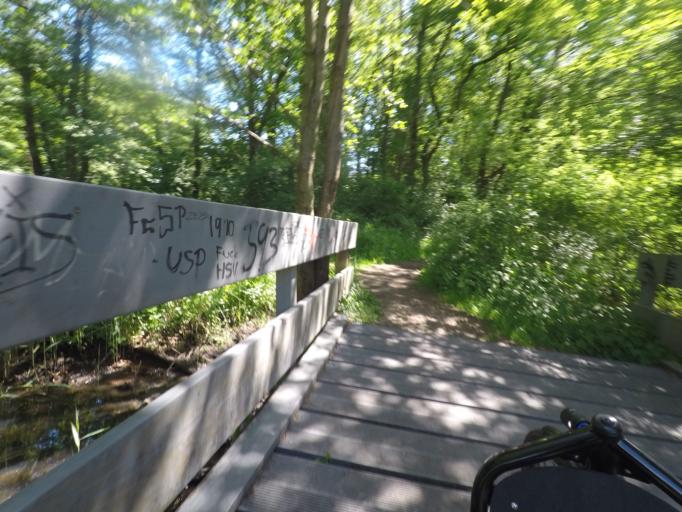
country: DE
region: Schleswig-Holstein
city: Stapelfeld
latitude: 53.6189
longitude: 10.1747
